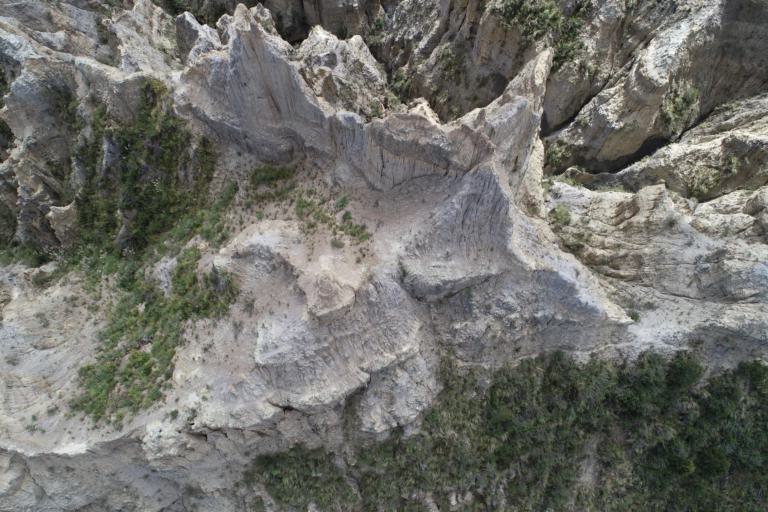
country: BO
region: La Paz
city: La Paz
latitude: -16.4995
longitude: -68.0642
